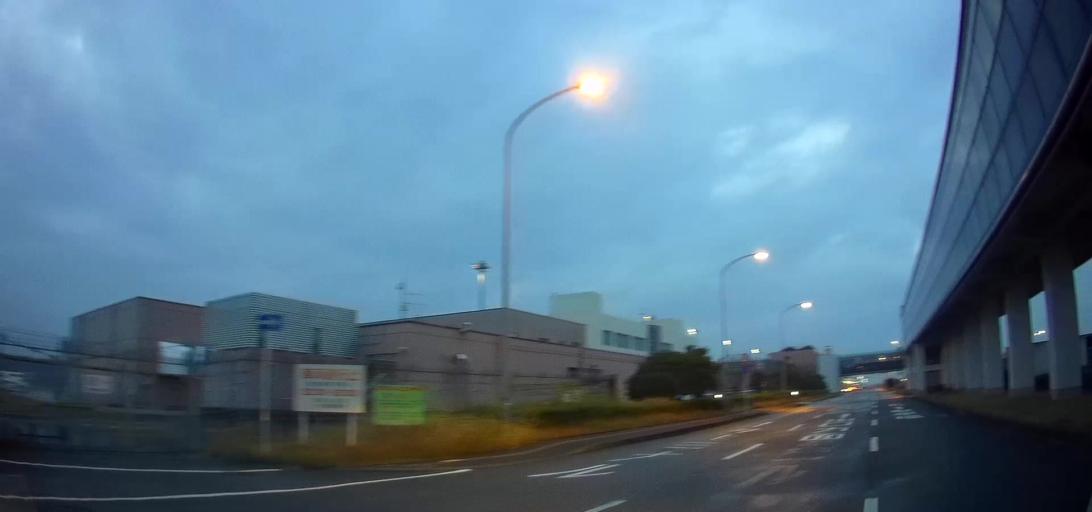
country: JP
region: Nagasaki
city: Omura
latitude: 32.9123
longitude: 129.9250
